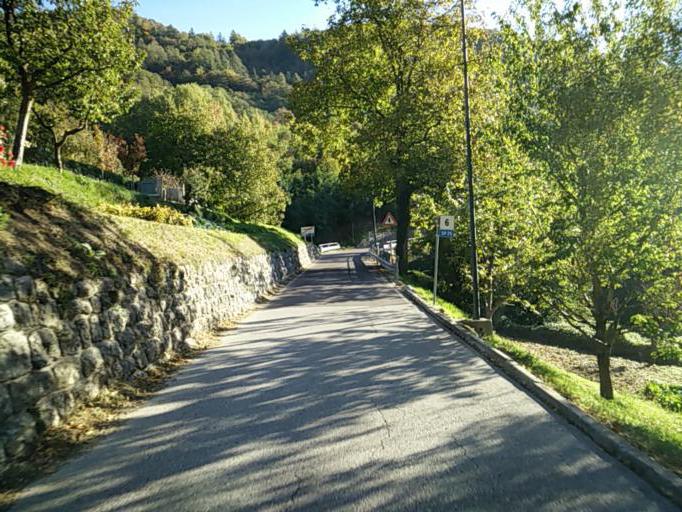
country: IT
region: Trentino-Alto Adige
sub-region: Provincia di Trento
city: Cimoneri
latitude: 45.9846
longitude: 11.0725
